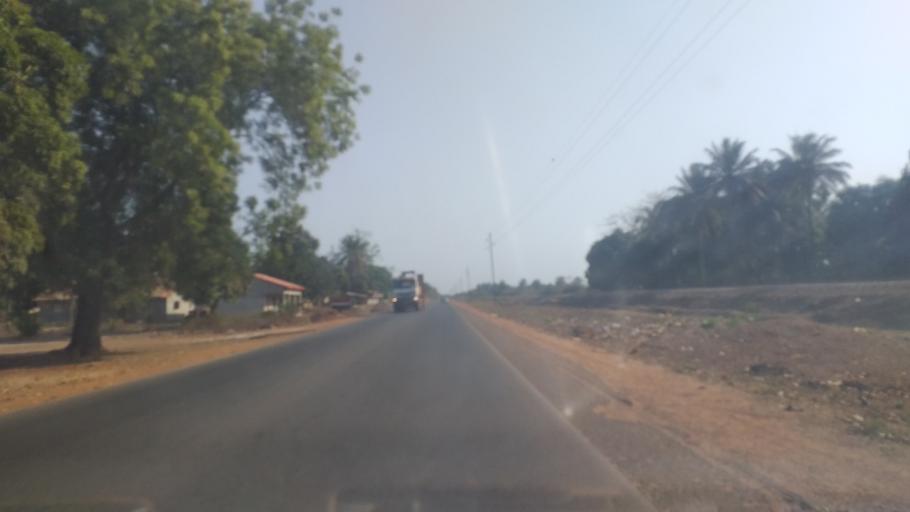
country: GN
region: Boke
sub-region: Boke Prefecture
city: Kamsar
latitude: 10.7180
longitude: -14.5214
